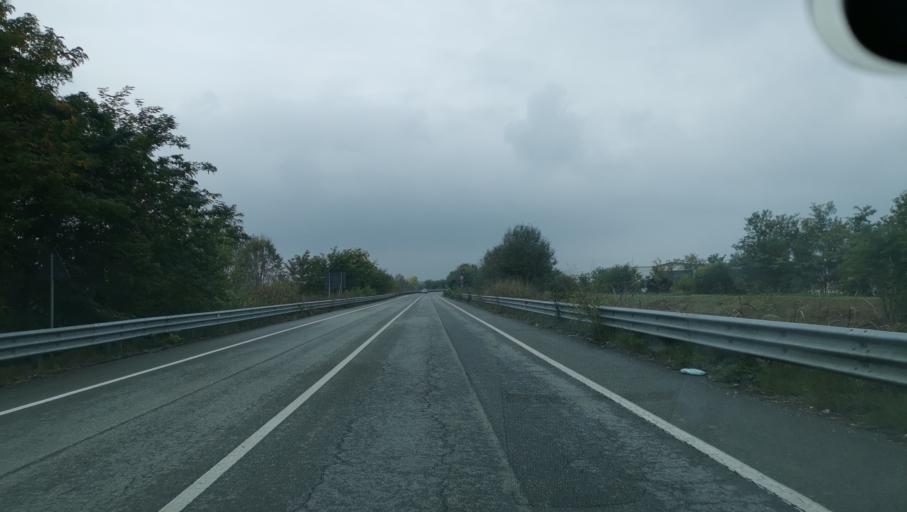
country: IT
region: Piedmont
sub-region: Provincia di Torino
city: San Raffaele Cimena
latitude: 45.1443
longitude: 7.8388
